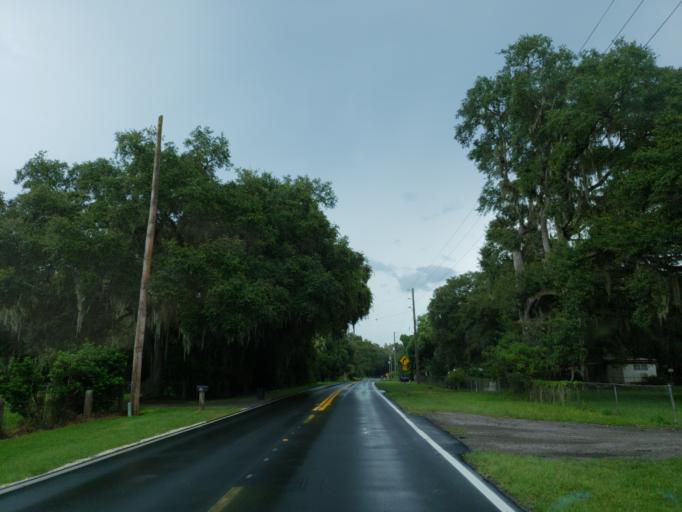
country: US
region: Florida
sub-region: Pasco County
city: Land O' Lakes
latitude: 28.2819
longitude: -82.4359
